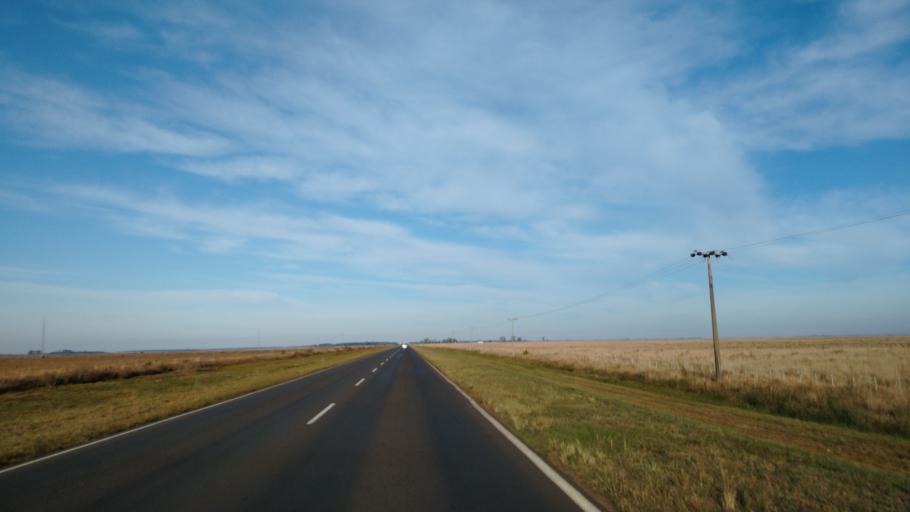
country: AR
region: Corrientes
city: La Cruz
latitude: -29.2171
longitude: -56.7077
